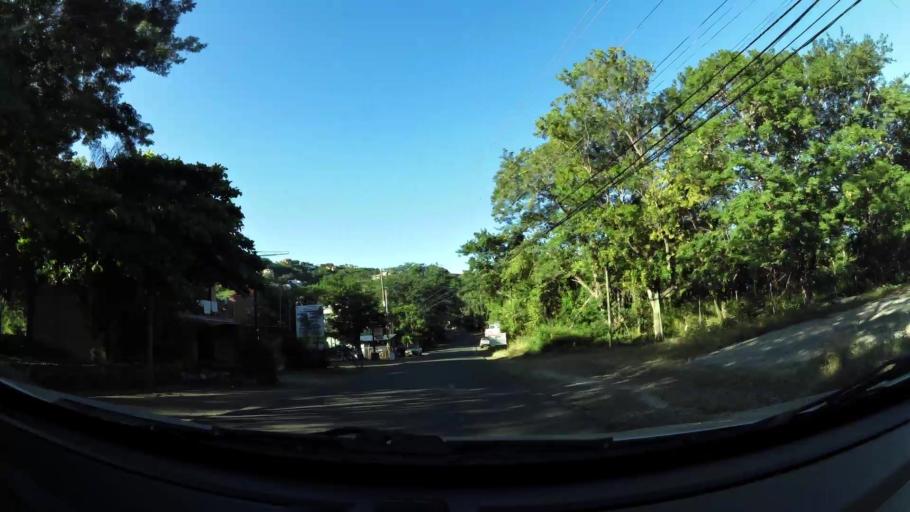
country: CR
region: Guanacaste
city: Sardinal
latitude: 10.5684
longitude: -85.6751
